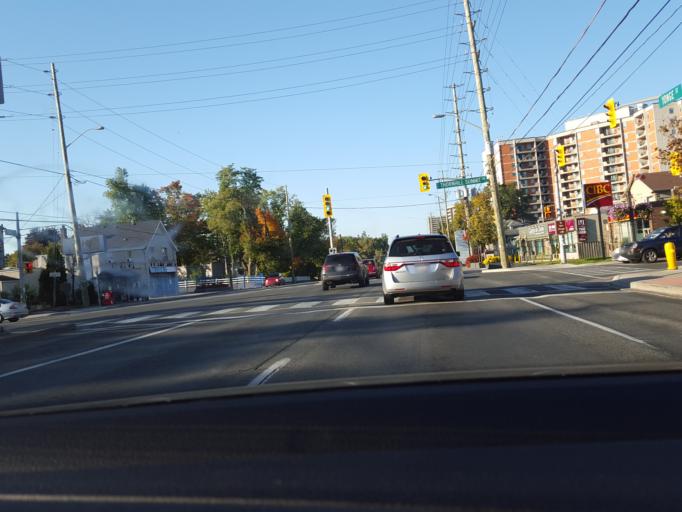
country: CA
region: Ontario
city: North York
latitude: 43.8160
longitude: -79.4243
